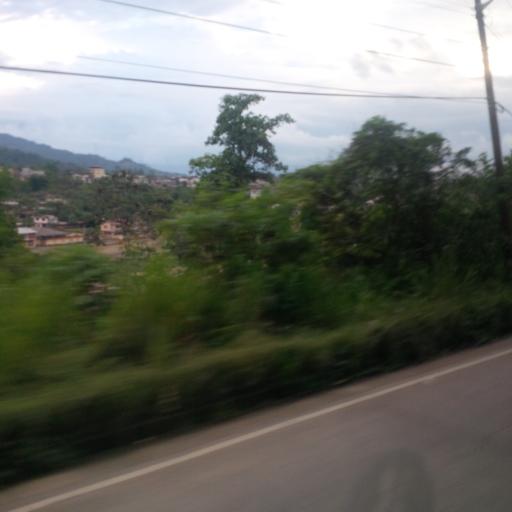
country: EC
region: Chimborazo
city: Alausi
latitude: -2.2020
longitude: -79.1276
